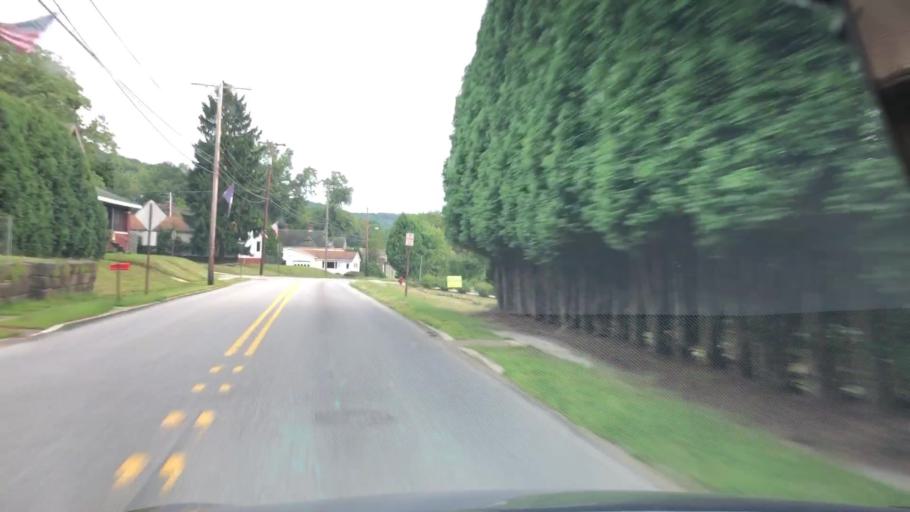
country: US
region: Pennsylvania
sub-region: Venango County
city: Hasson Heights
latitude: 41.4714
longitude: -79.6924
